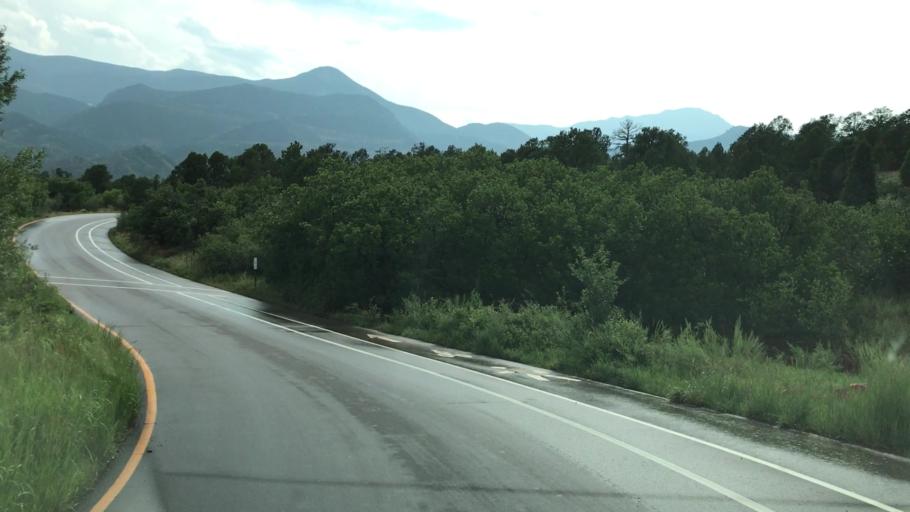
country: US
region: Colorado
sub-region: El Paso County
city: Manitou Springs
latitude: 38.8675
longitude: -104.8913
